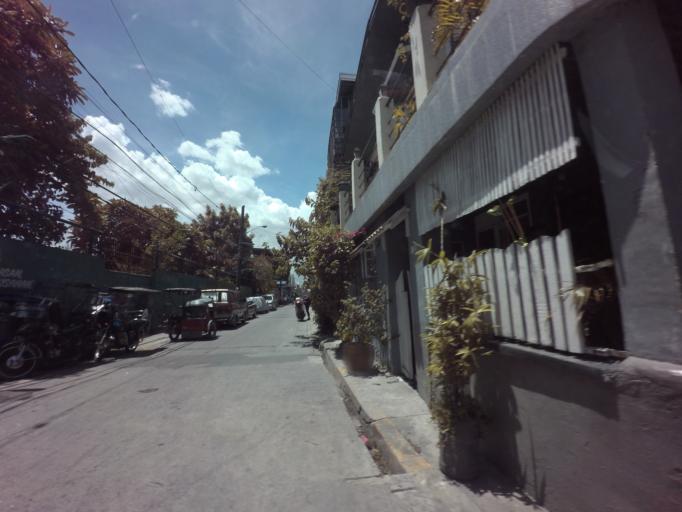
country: PH
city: Sambayanihan People's Village
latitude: 14.4946
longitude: 120.9900
